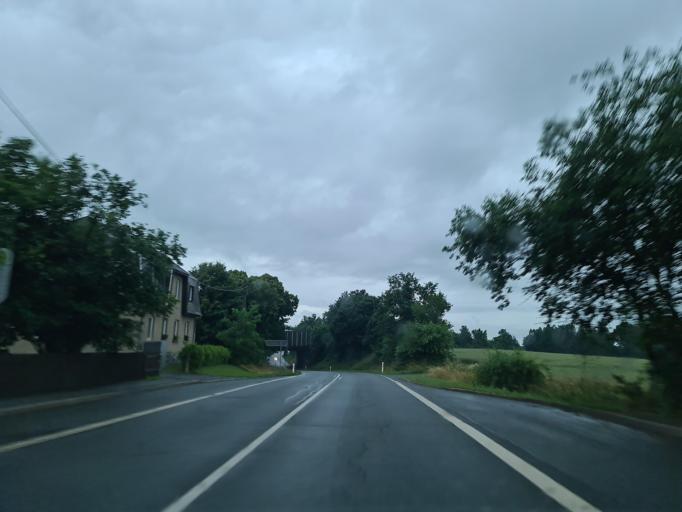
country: DE
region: Saxony
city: Limbach
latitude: 50.5398
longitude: 12.2550
